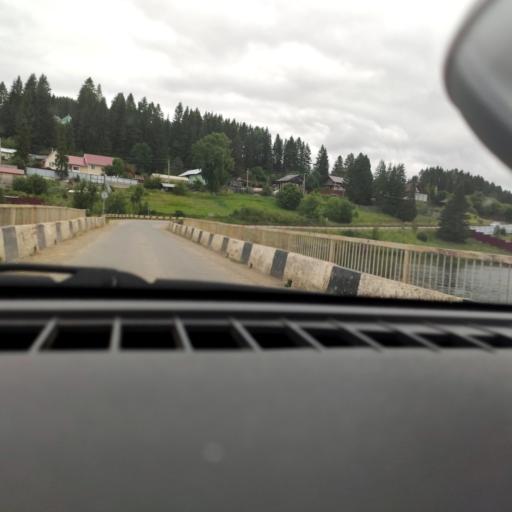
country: RU
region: Perm
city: Polazna
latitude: 58.3478
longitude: 56.2465
